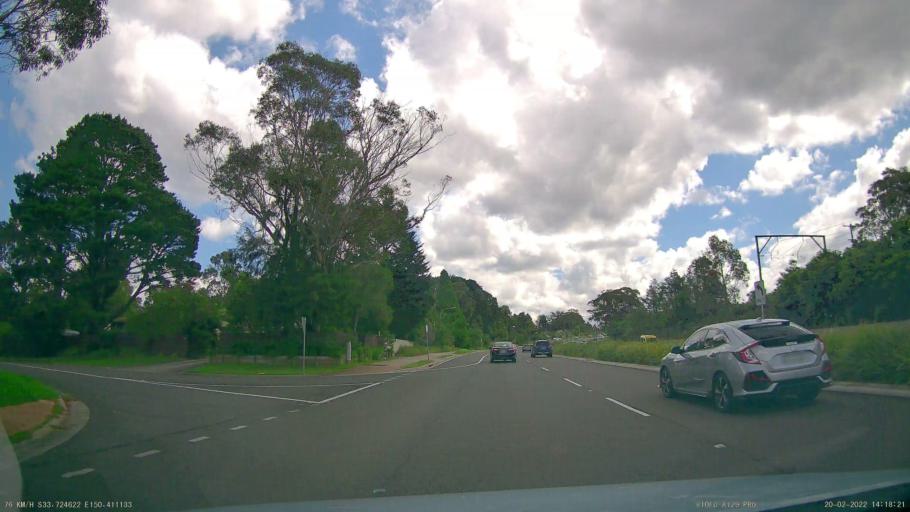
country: AU
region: New South Wales
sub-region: Blue Mountains Municipality
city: Lawson
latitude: -33.7250
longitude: 150.4105
